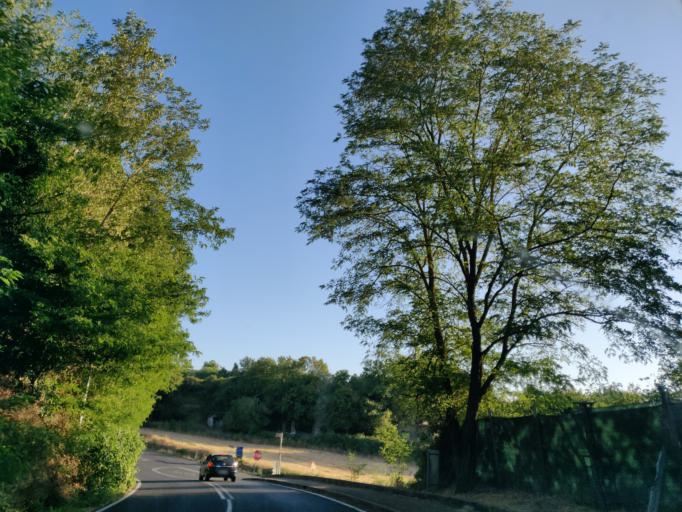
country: IT
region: Latium
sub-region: Provincia di Viterbo
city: Grotte di Castro
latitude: 42.6731
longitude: 11.8605
